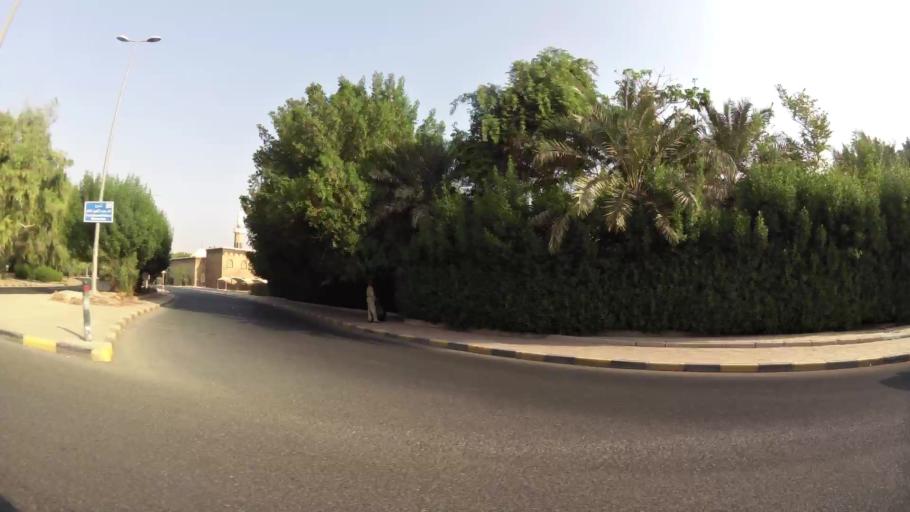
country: KW
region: Mubarak al Kabir
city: Sabah as Salim
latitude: 29.2725
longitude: 48.0661
